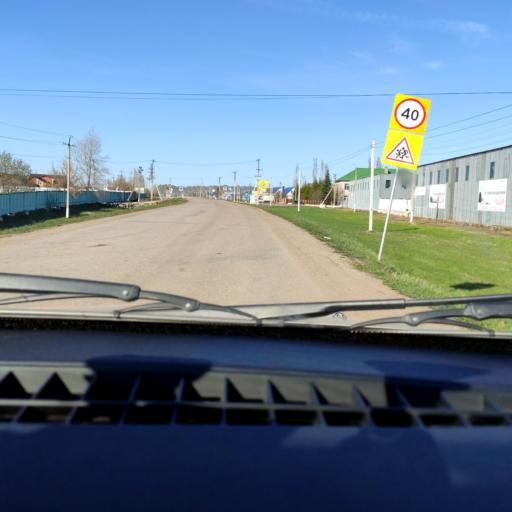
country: RU
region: Bashkortostan
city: Kabakovo
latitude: 54.5975
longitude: 56.1814
